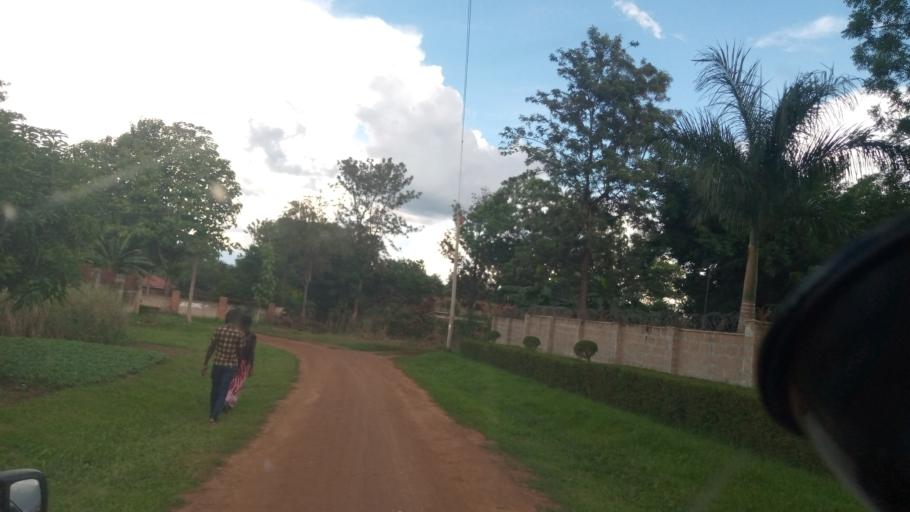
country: UG
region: Northern Region
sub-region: Lira District
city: Lira
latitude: 2.2382
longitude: 32.9066
